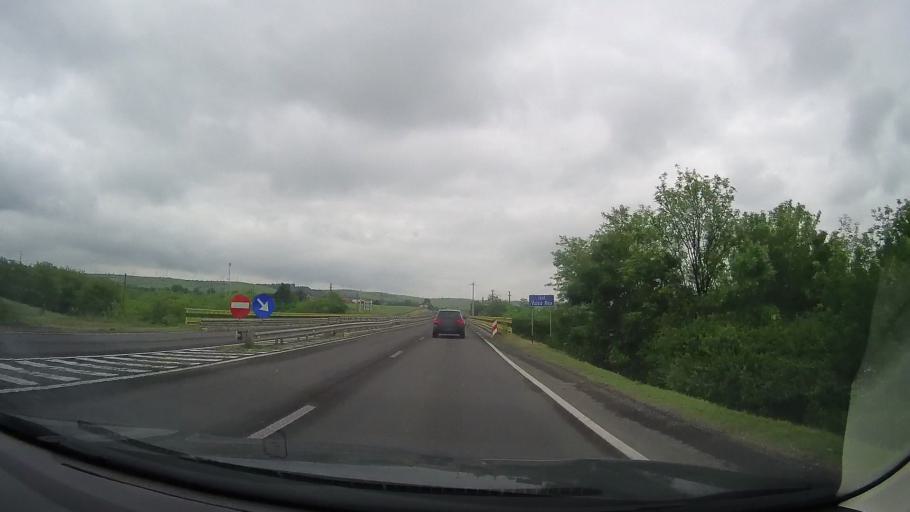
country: RO
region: Dolj
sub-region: Comuna Bradesti
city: Bradesti
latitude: 44.5005
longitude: 23.6048
